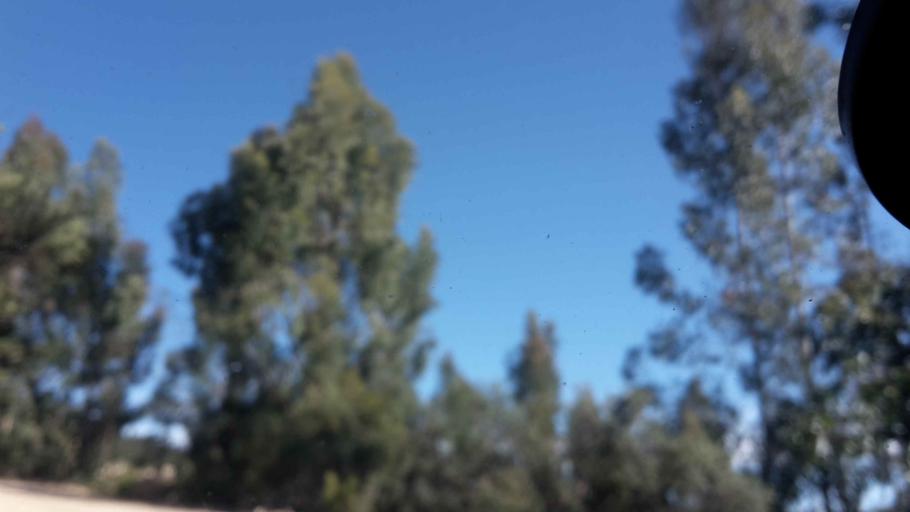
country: BO
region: Cochabamba
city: Arani
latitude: -17.6745
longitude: -65.7286
